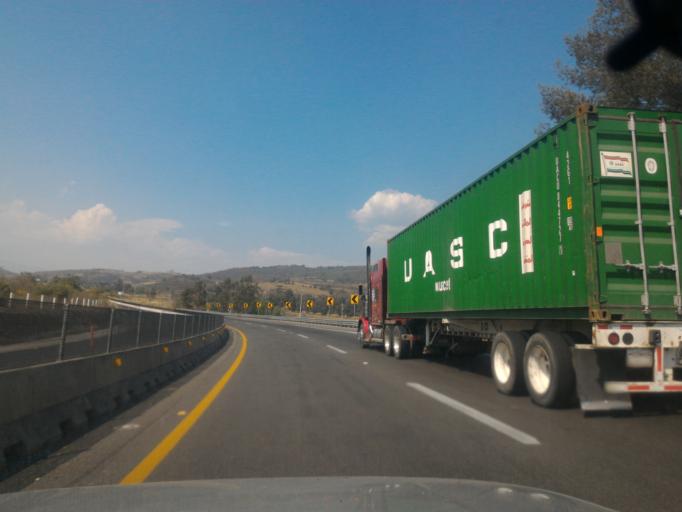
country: MX
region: Jalisco
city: San Andres Ixtlan
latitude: 19.8230
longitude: -103.4945
